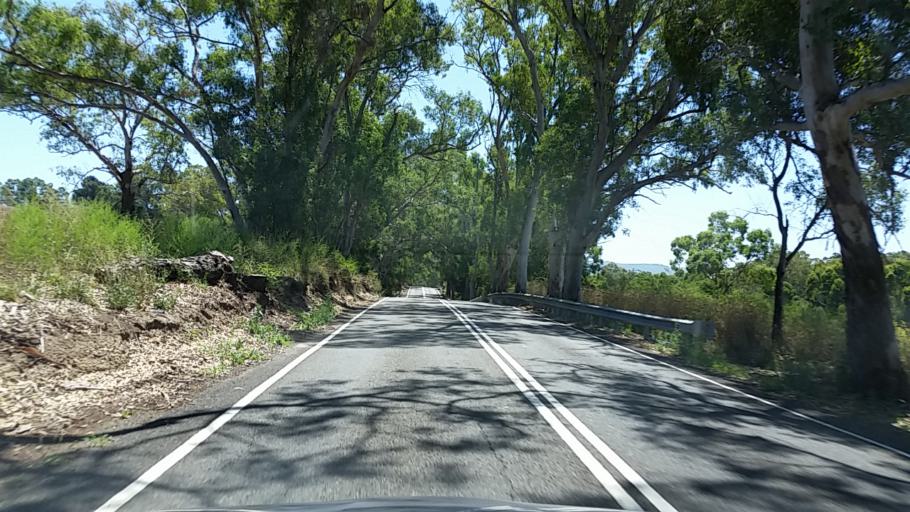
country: AU
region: South Australia
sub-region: Adelaide Hills
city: Balhannah
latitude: -35.0025
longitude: 138.8387
